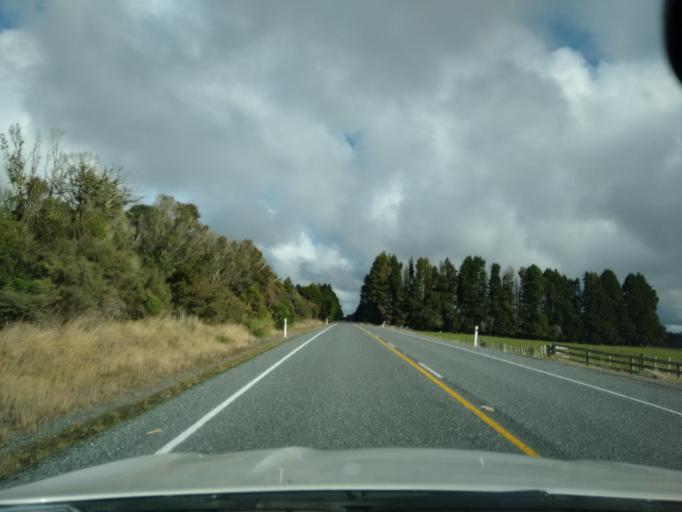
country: NZ
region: Manawatu-Wanganui
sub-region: Ruapehu District
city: Waiouru
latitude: -39.2822
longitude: 175.3863
